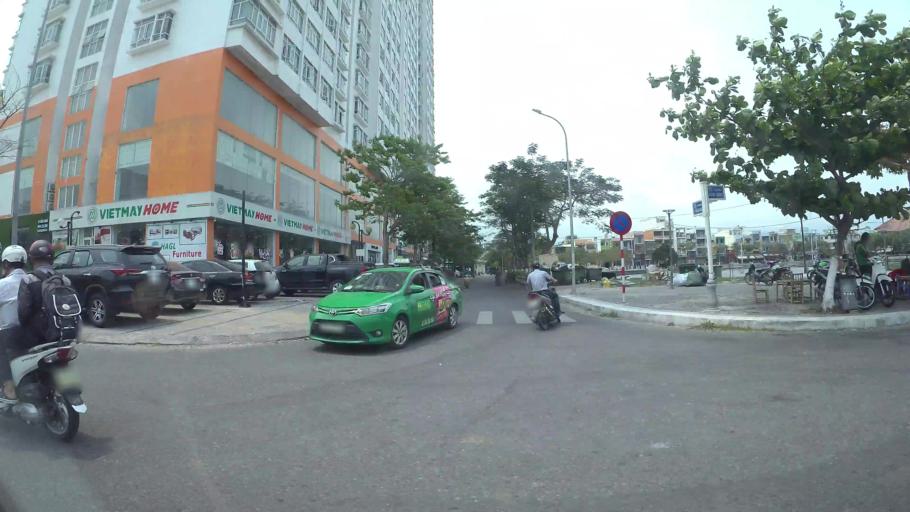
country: VN
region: Da Nang
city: Da Nang
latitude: 16.0629
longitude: 108.2106
